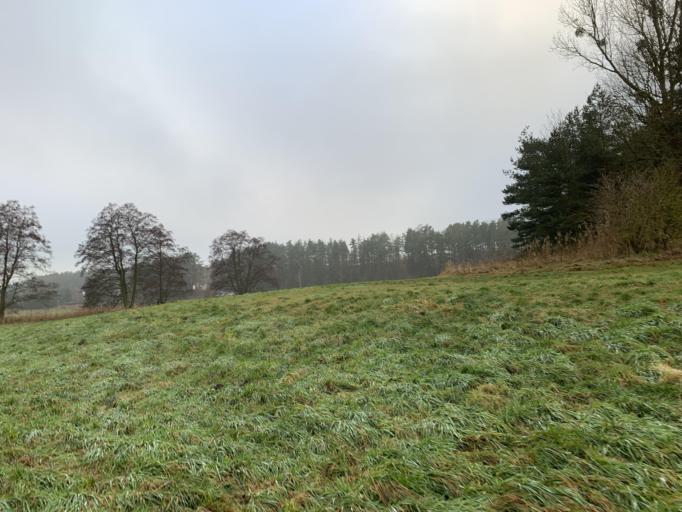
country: DE
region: Mecklenburg-Vorpommern
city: Blankensee
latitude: 53.4031
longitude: 13.2764
